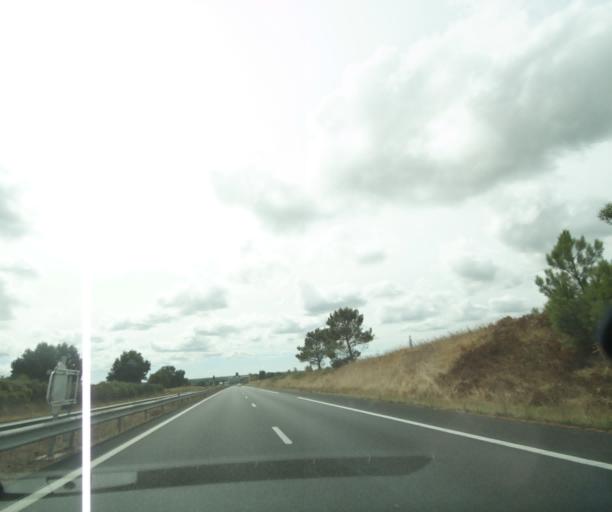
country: FR
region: Aquitaine
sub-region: Departement de la Gironde
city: Marcillac
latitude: 45.2820
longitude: -0.5509
